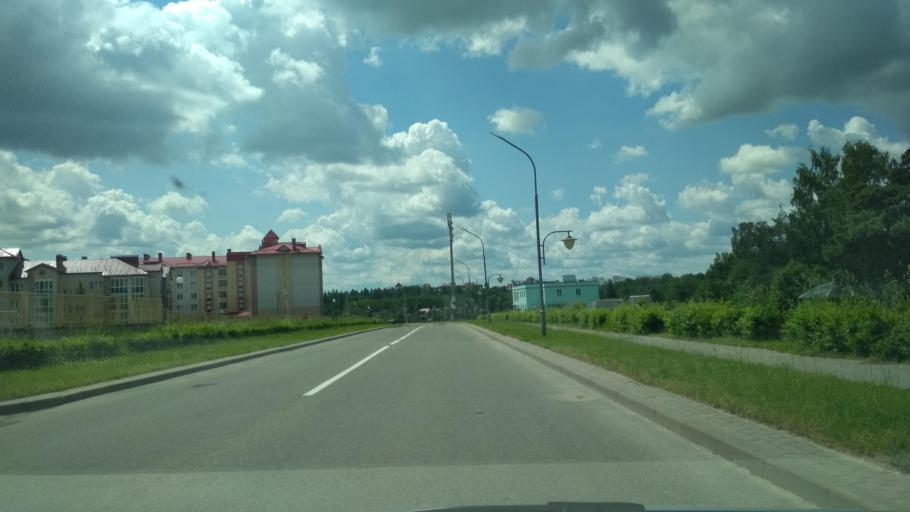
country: BY
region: Grodnenskaya
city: Astravyets
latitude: 54.6169
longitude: 25.9767
